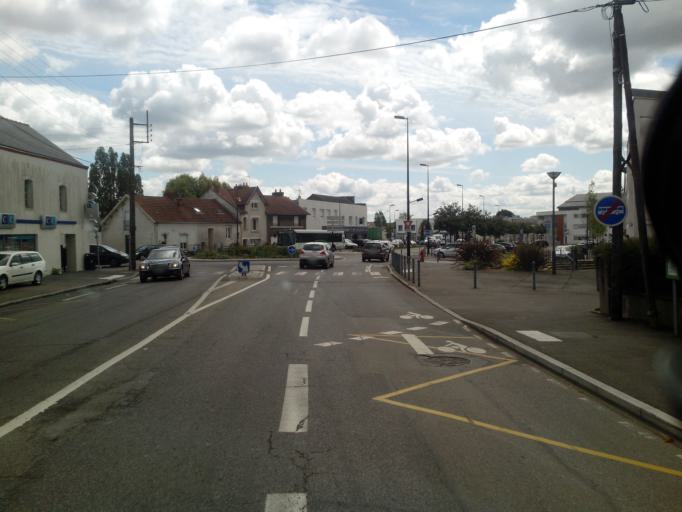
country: FR
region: Pays de la Loire
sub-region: Departement de la Loire-Atlantique
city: Nantes
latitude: 47.2546
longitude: -1.5769
